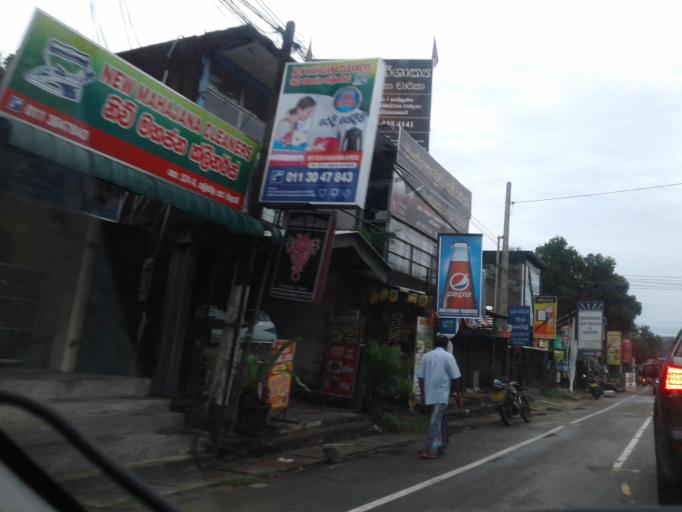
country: LK
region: Western
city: Mulleriyawa
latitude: 6.9042
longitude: 79.9606
